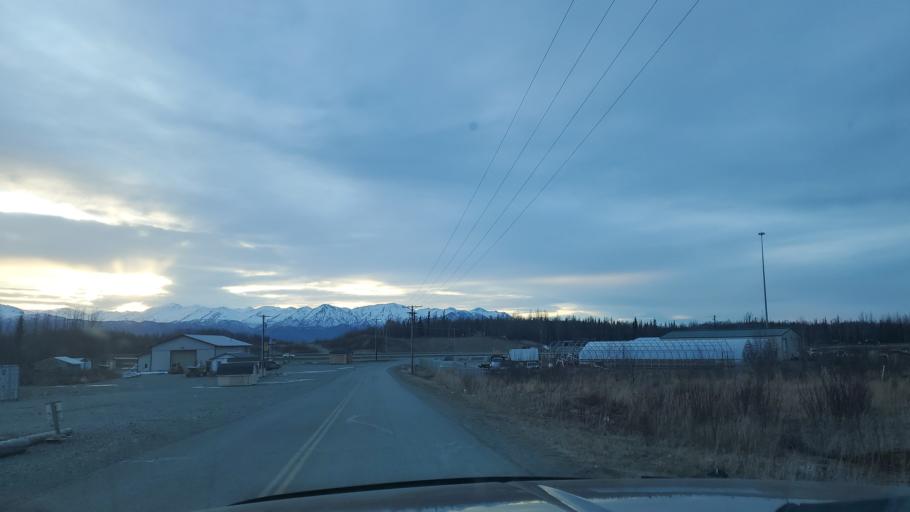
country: US
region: Alaska
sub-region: Matanuska-Susitna Borough
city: Lakes
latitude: 61.5725
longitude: -149.3448
